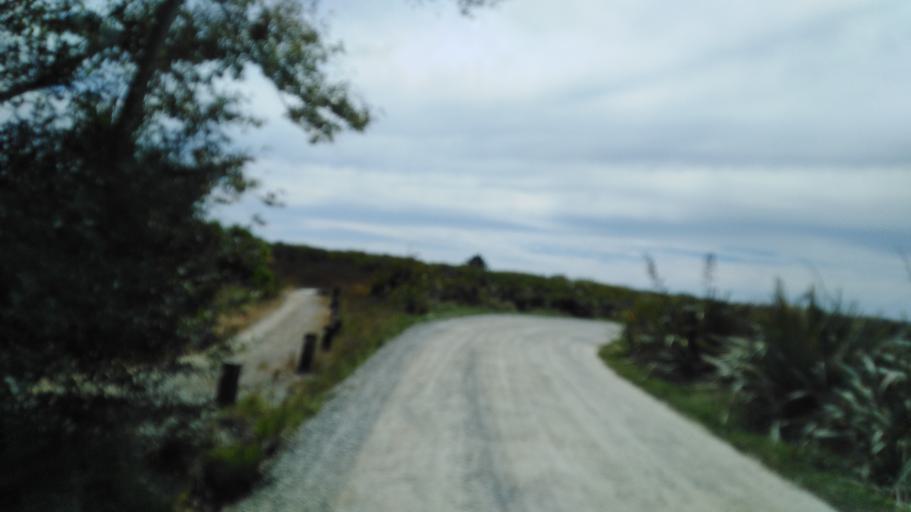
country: NZ
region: West Coast
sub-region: Buller District
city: Westport
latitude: -41.7372
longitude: 171.6043
